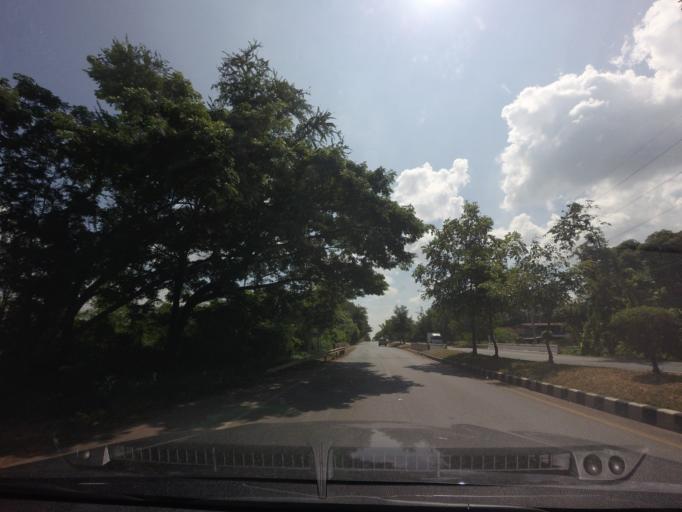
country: TH
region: Phetchabun
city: Nong Phai
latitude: 16.0369
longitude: 101.0783
